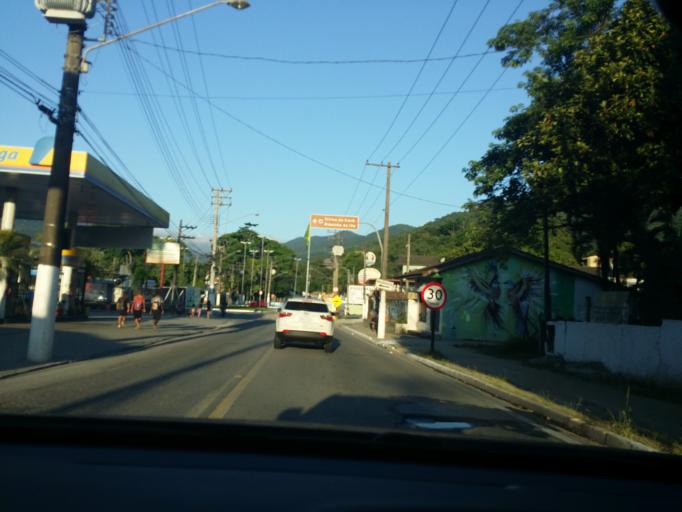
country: BR
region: Sao Paulo
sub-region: Sao Sebastiao
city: Sao Sebastiao
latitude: -23.7840
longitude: -45.6226
